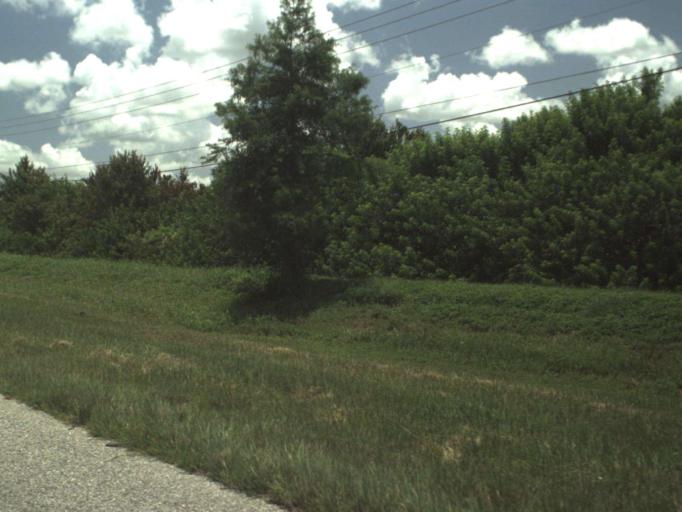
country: US
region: Florida
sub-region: Indian River County
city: Fellsmere
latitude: 27.6404
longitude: -80.6554
